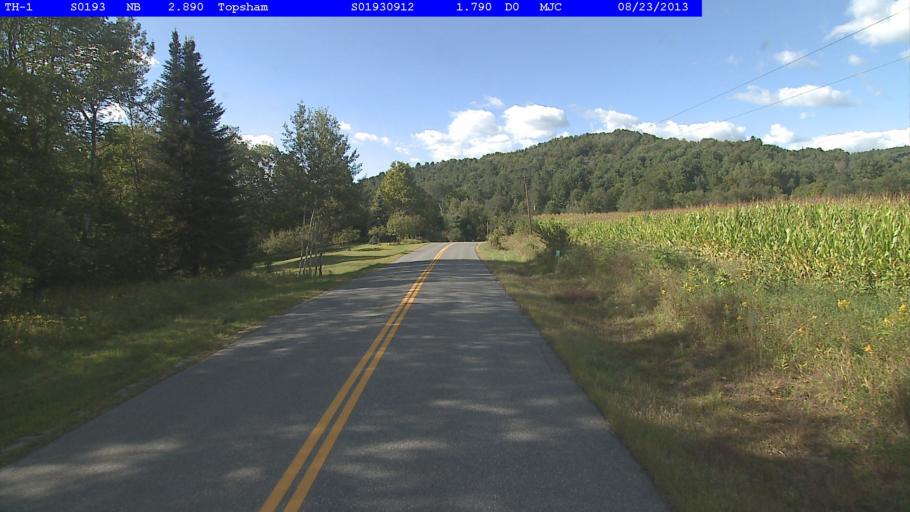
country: US
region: New Hampshire
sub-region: Grafton County
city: Haverhill
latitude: 44.0957
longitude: -72.2230
